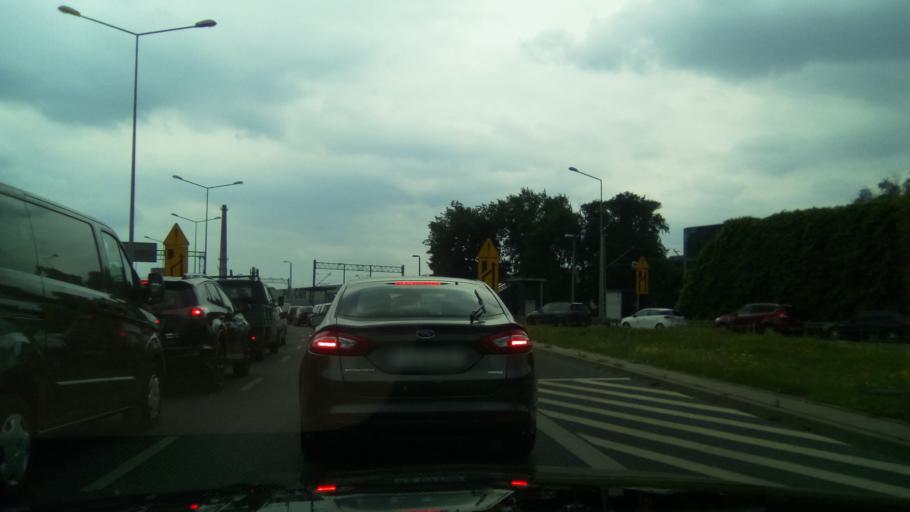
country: PL
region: Greater Poland Voivodeship
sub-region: Powiat poznanski
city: Swarzedz
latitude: 52.4103
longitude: 17.0278
